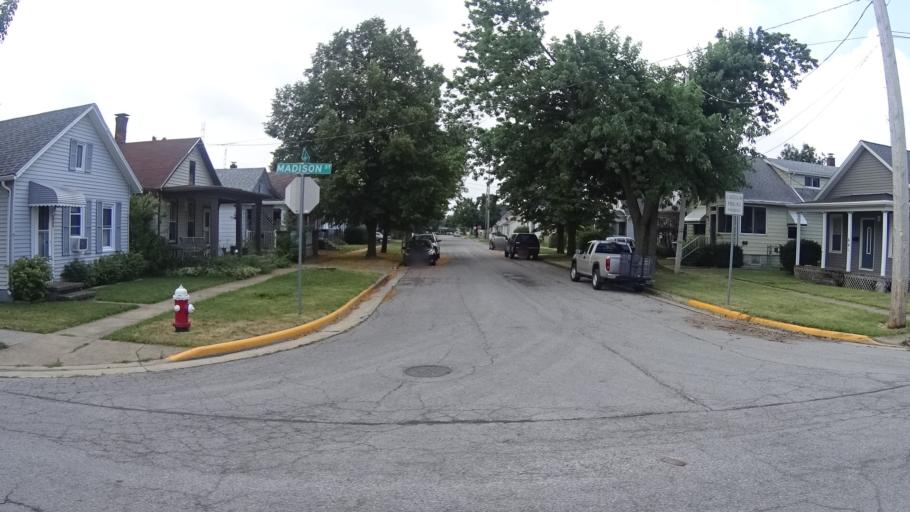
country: US
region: Ohio
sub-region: Erie County
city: Sandusky
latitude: 41.4476
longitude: -82.7288
